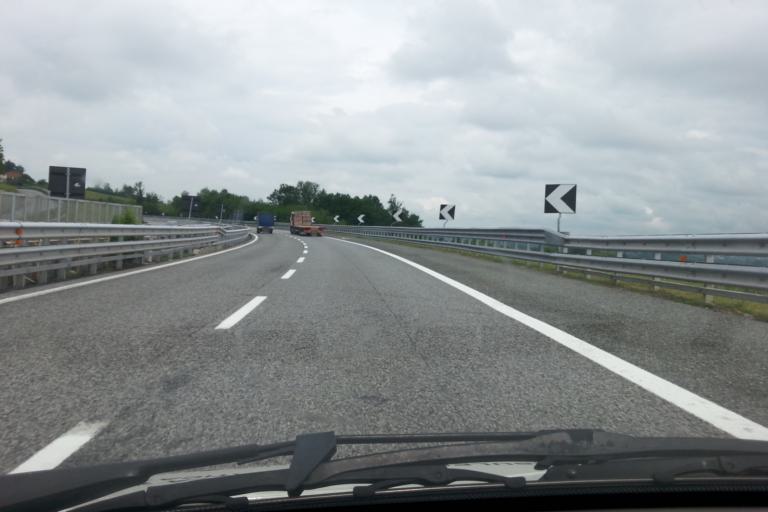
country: IT
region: Piedmont
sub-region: Provincia di Cuneo
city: Bastia Mondovi
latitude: 44.4231
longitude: 7.8868
